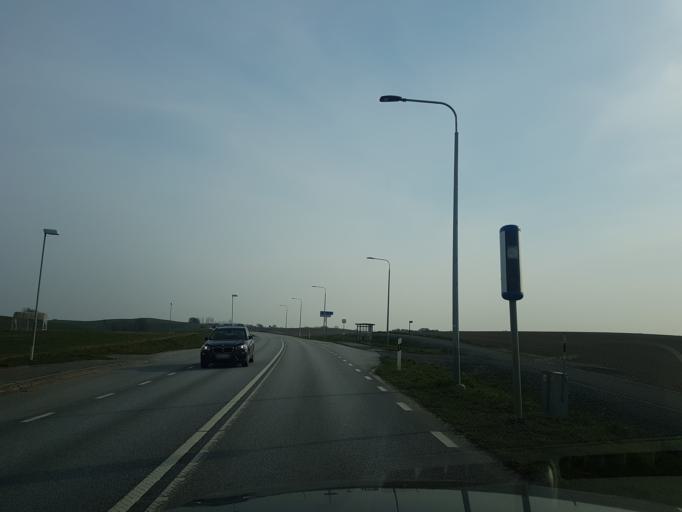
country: SE
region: Skane
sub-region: Ystads Kommun
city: Ystad
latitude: 55.4697
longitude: 13.7970
